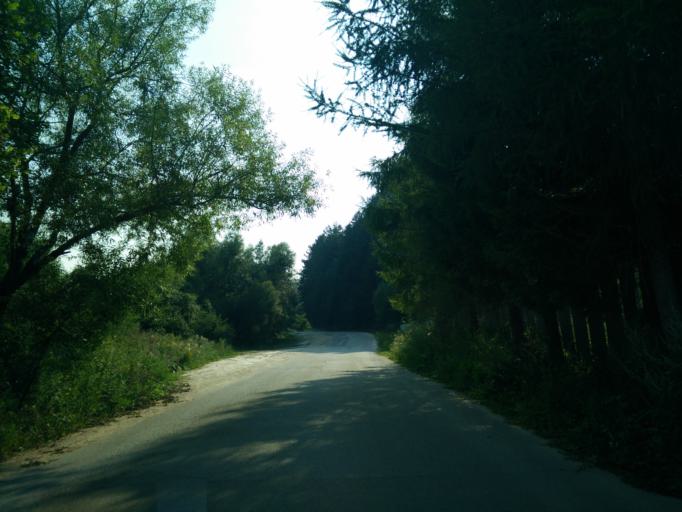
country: SK
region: Zilinsky
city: Rajec
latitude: 49.0661
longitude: 18.6249
